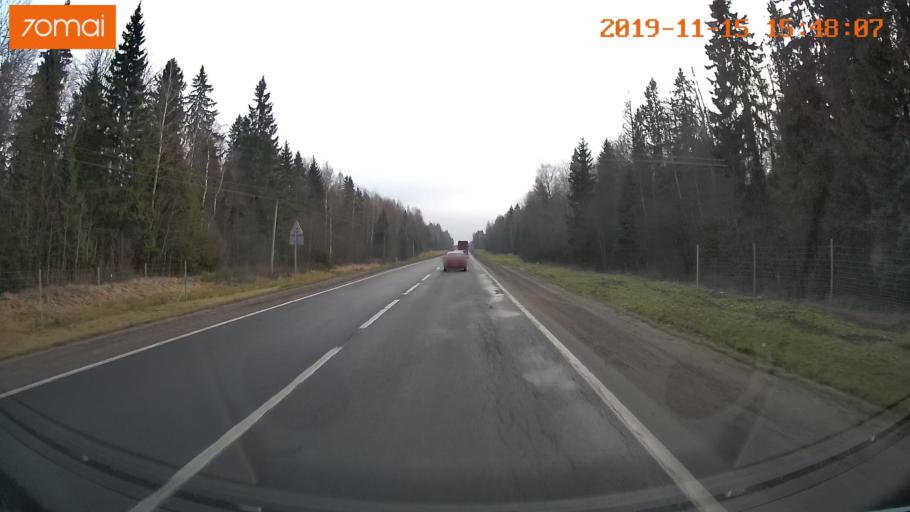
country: RU
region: Jaroslavl
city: Danilov
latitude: 57.9308
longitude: 40.0065
